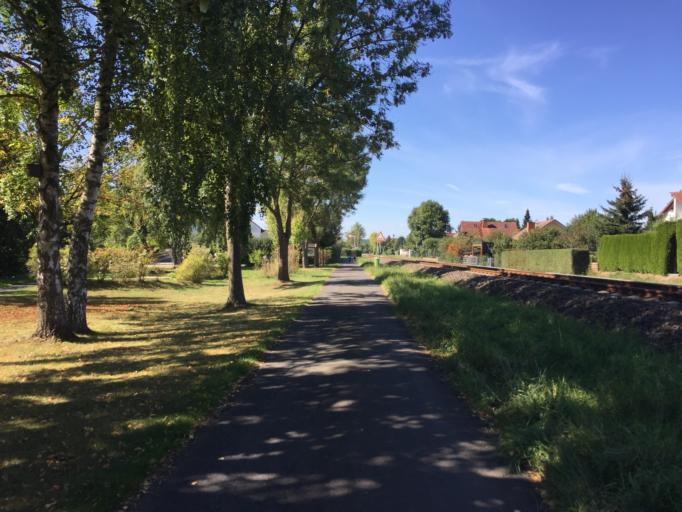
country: DE
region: Hesse
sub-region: Regierungsbezirk Giessen
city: Reiskirchen
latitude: 50.5944
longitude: 8.8567
